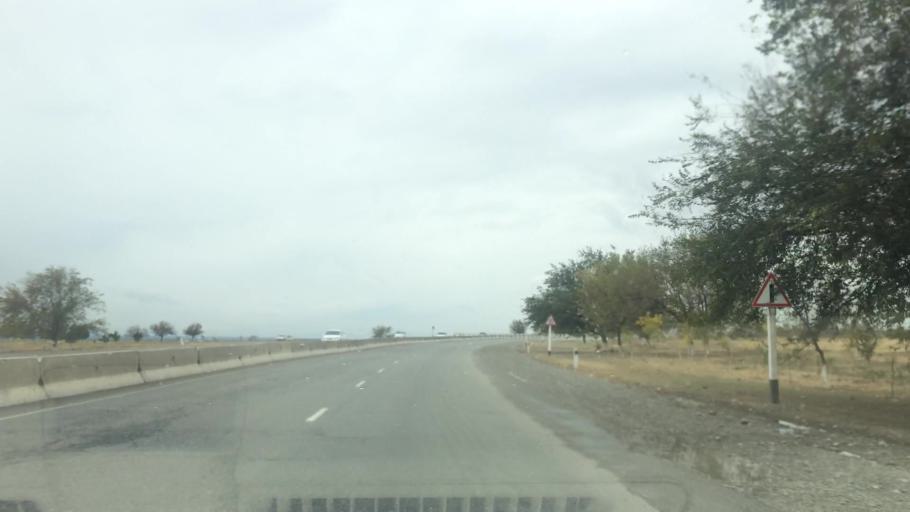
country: UZ
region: Samarqand
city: Bulung'ur
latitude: 39.8378
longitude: 67.4459
